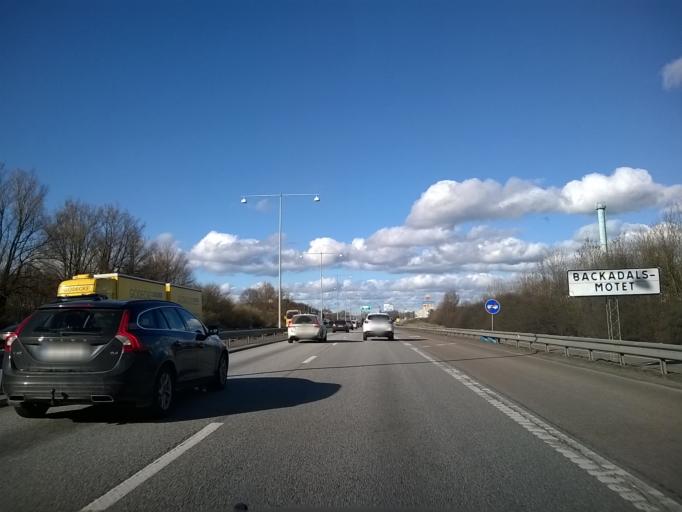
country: SE
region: Vaestra Goetaland
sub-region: Goteborg
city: Goeteborg
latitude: 57.7433
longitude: 11.9888
